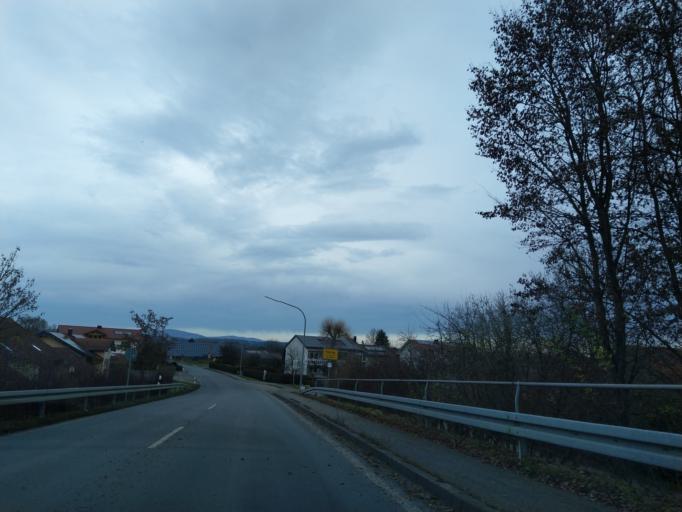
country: DE
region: Bavaria
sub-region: Lower Bavaria
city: Kunzing
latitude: 48.6652
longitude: 13.0705
